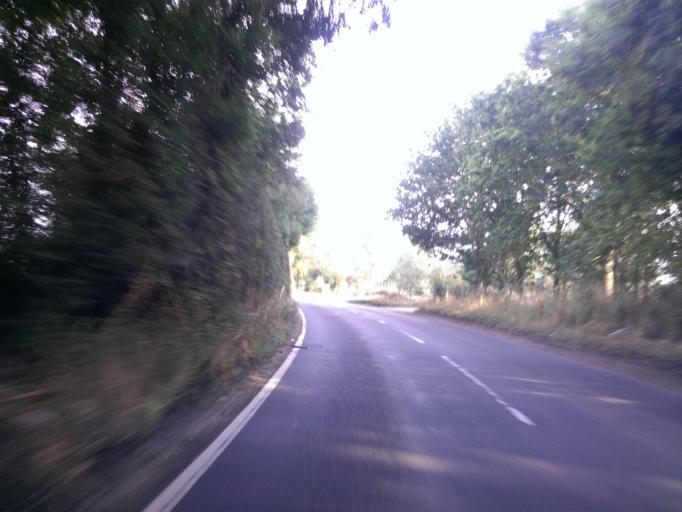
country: GB
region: England
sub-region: Essex
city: Witham
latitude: 51.8116
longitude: 0.6719
